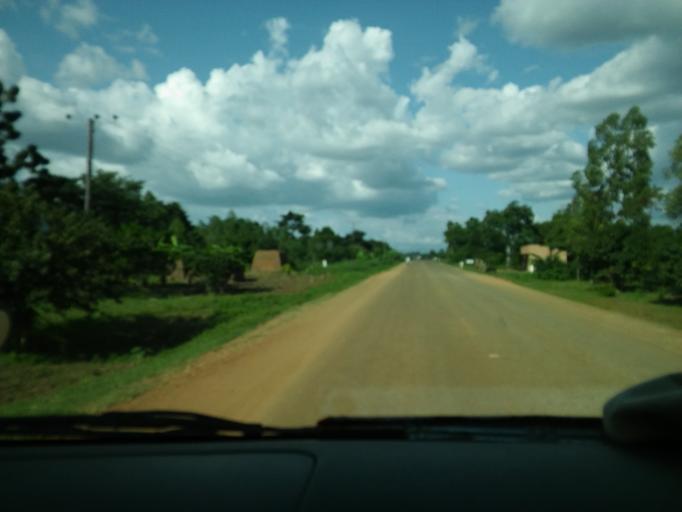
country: UG
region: Eastern Region
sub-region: Budaka District
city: Budaka
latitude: 1.0166
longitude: 33.8606
